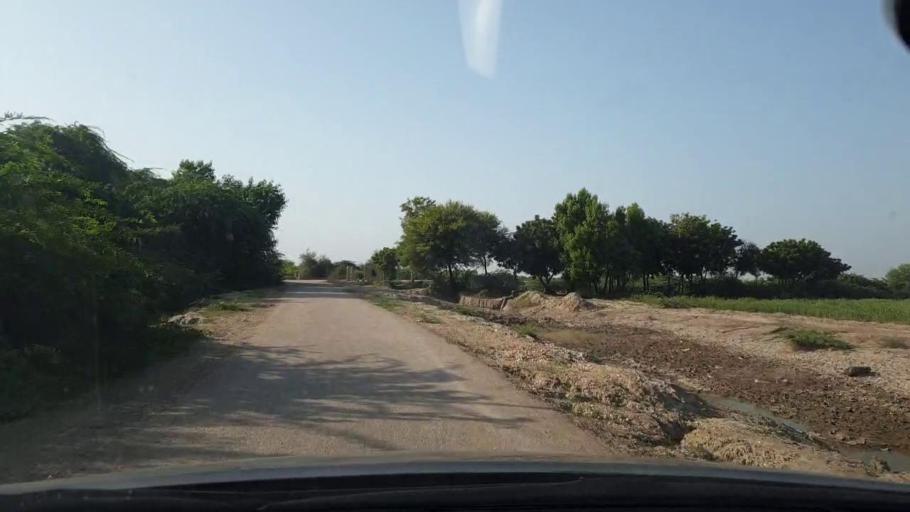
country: PK
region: Sindh
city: Naukot
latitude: 24.8391
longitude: 69.2223
